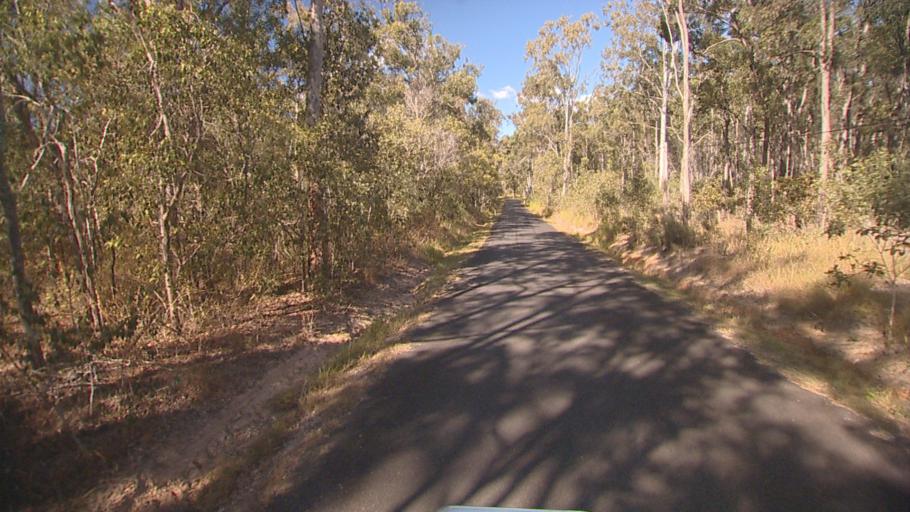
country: AU
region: Queensland
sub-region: Ipswich
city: Springfield Lakes
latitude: -27.7390
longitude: 152.9377
